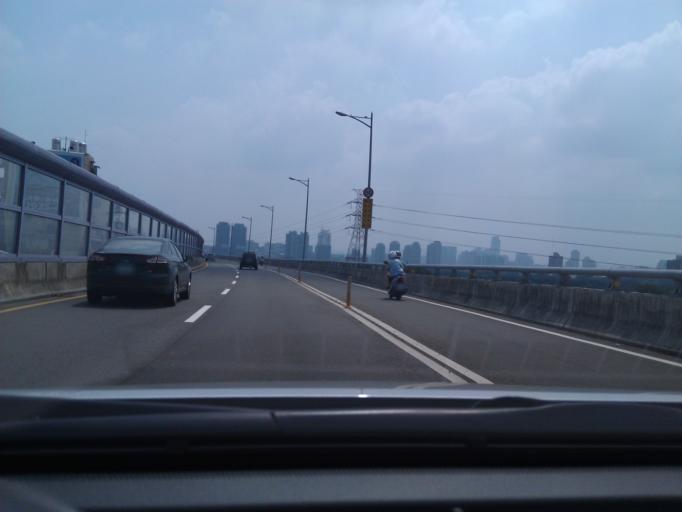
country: TW
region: Taipei
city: Taipei
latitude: 25.0174
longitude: 121.5099
